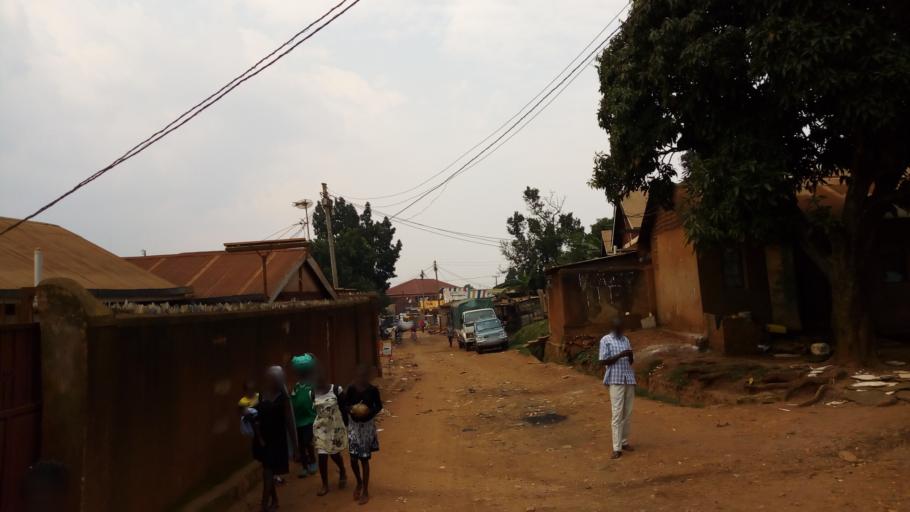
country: UG
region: Central Region
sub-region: Wakiso District
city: Kireka
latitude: 0.3209
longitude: 32.6393
